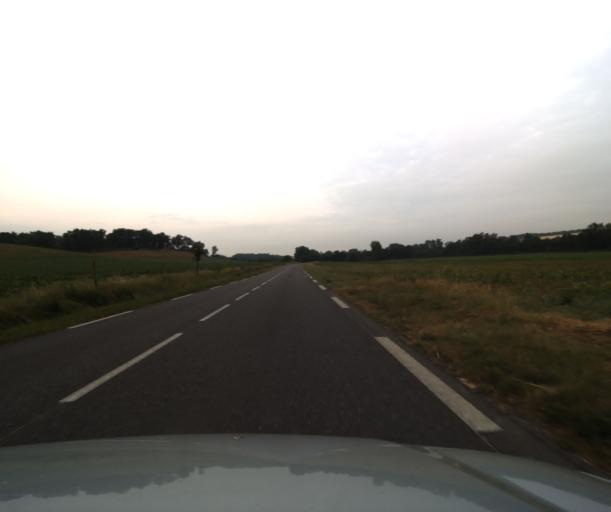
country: FR
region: Midi-Pyrenees
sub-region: Departement du Gers
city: Gimont
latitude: 43.7192
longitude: 0.8687
